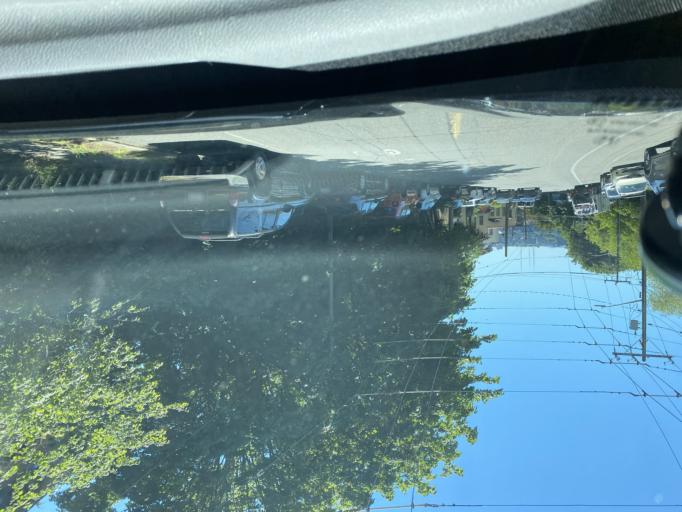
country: US
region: Washington
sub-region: King County
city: Seattle
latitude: 47.6347
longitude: -122.3475
